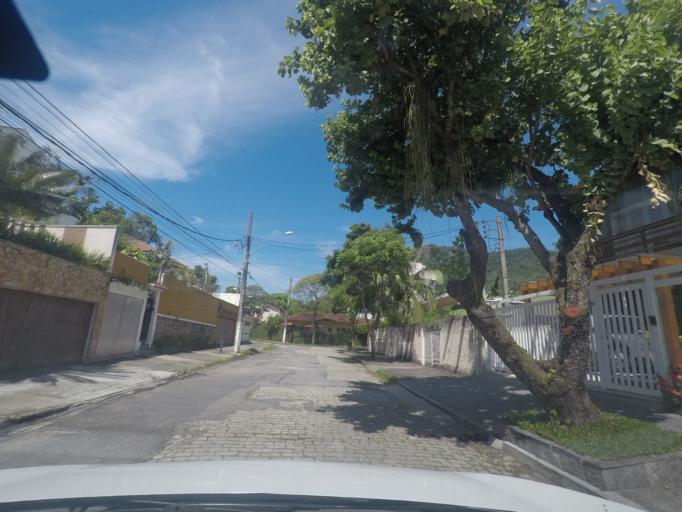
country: BR
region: Rio de Janeiro
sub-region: Niteroi
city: Niteroi
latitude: -22.9190
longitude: -43.0883
